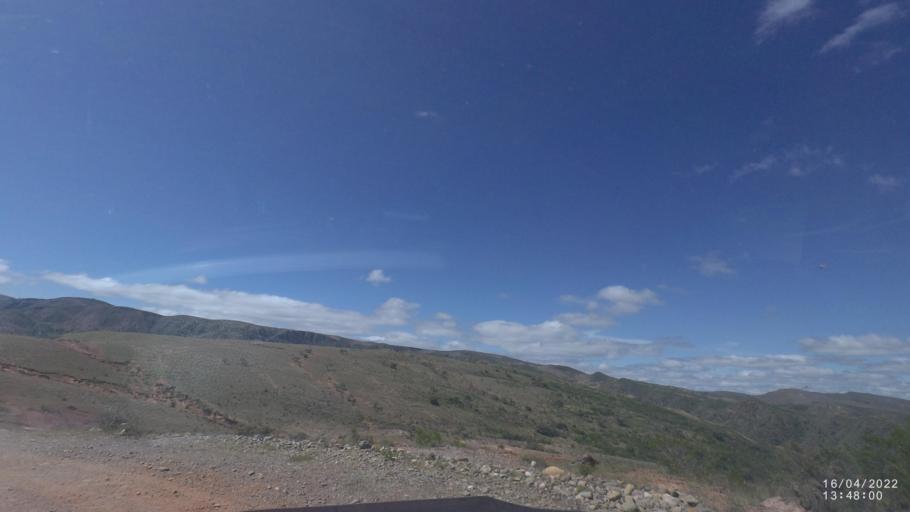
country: BO
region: Cochabamba
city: Mizque
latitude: -18.0109
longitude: -65.5802
